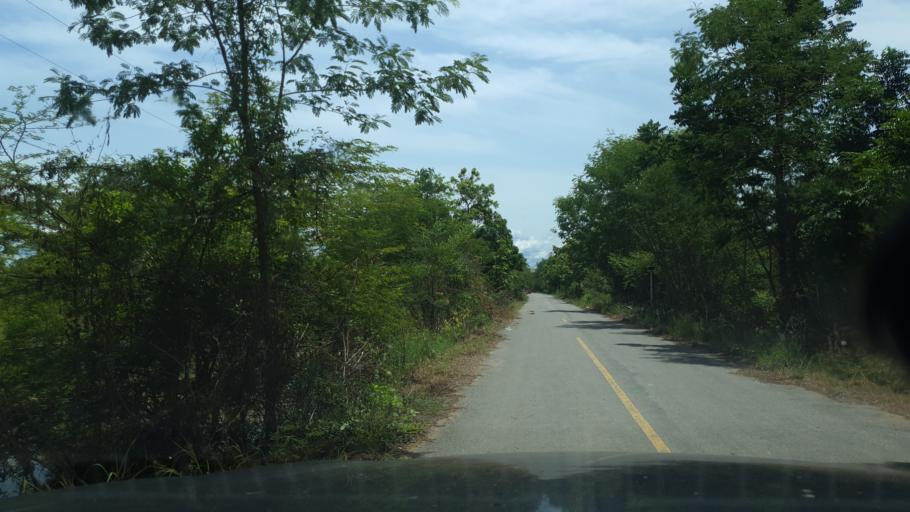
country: TH
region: Sukhothai
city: Ban Na
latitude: 17.1084
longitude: 99.6782
